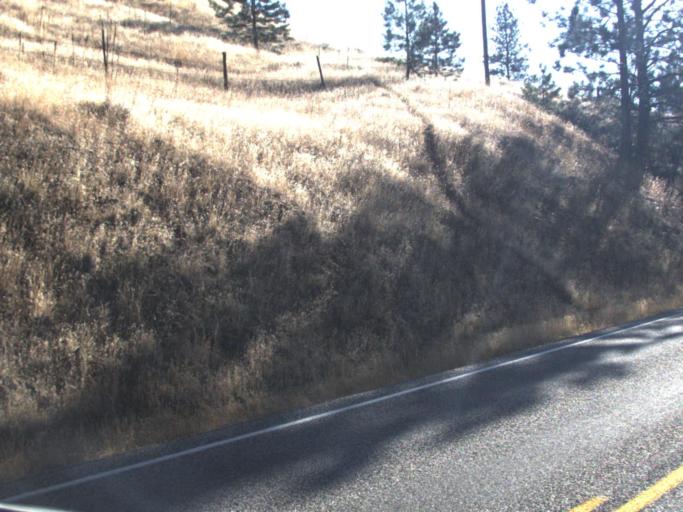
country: CA
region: British Columbia
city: Grand Forks
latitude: 48.8567
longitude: -118.6041
